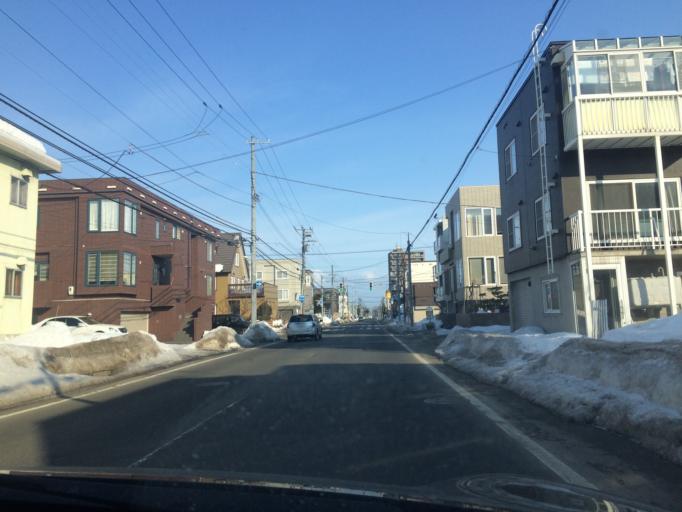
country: JP
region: Hokkaido
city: Sapporo
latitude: 43.0829
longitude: 141.3534
